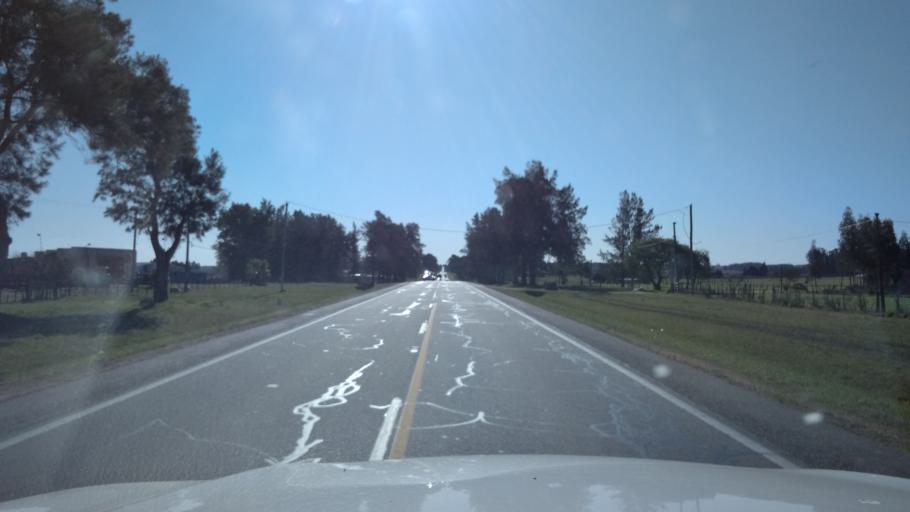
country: UY
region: Canelones
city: San Jacinto
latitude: -34.5844
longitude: -55.8411
